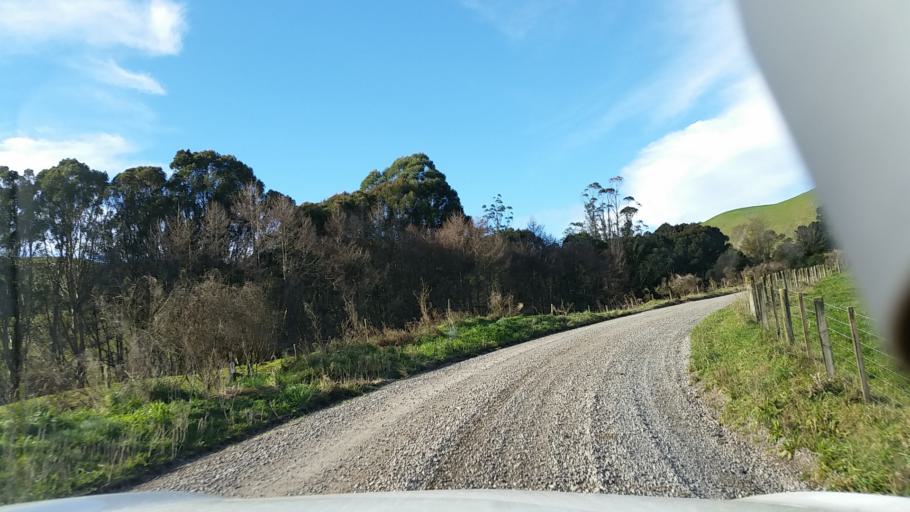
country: NZ
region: Bay of Plenty
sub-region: Rotorua District
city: Rotorua
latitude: -38.3580
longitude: 176.2145
